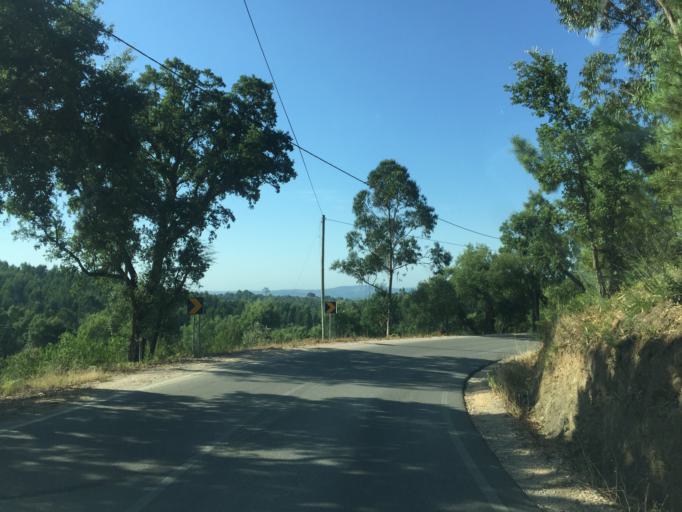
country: PT
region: Santarem
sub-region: Ferreira do Zezere
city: Ferreira do Zezere
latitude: 39.6012
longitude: -8.3134
